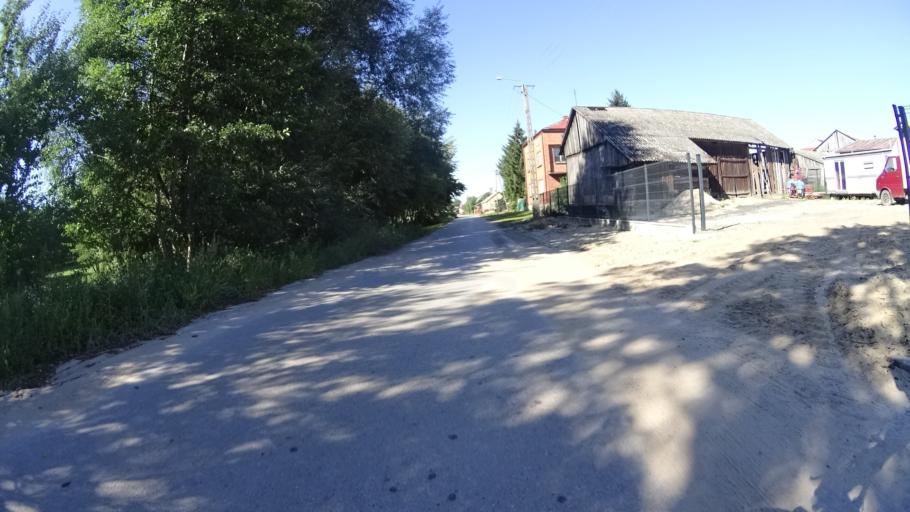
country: PL
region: Masovian Voivodeship
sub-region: Powiat bialobrzeski
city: Wysmierzyce
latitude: 51.6644
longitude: 20.8477
